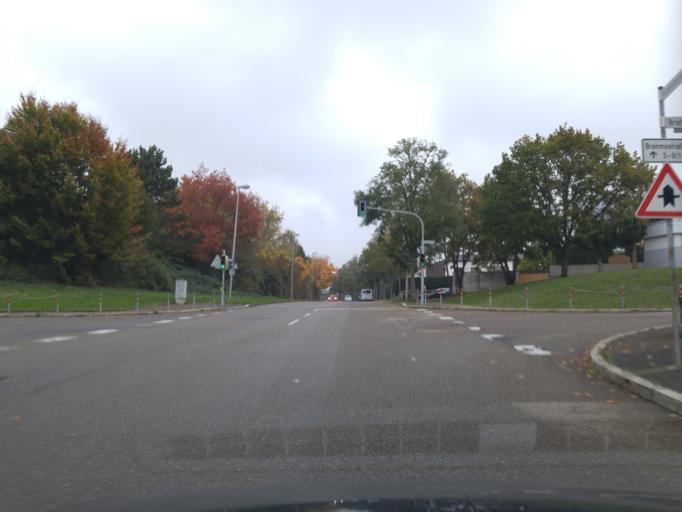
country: DE
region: Baden-Wuerttemberg
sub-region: Regierungsbezirk Stuttgart
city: Bad Wimpfen
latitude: 49.1969
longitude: 9.1501
